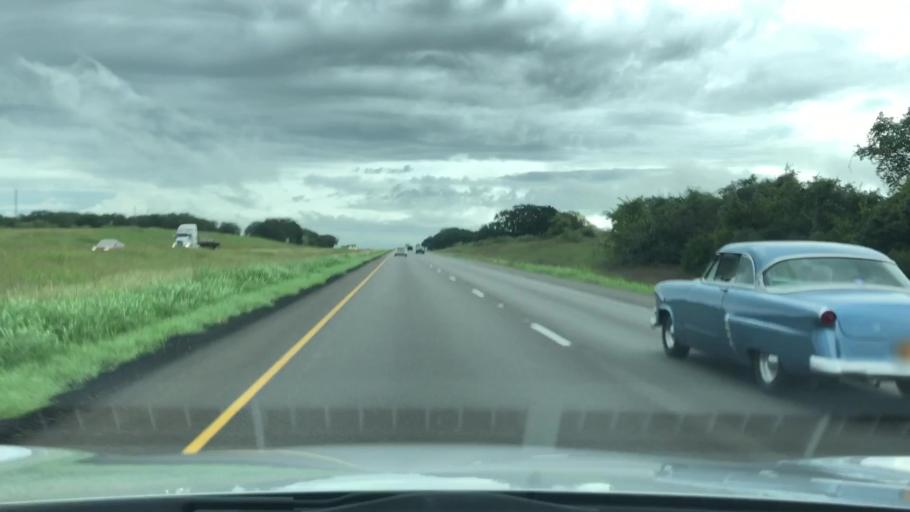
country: US
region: Texas
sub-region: Gonzales County
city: Waelder
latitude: 29.6568
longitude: -97.4285
